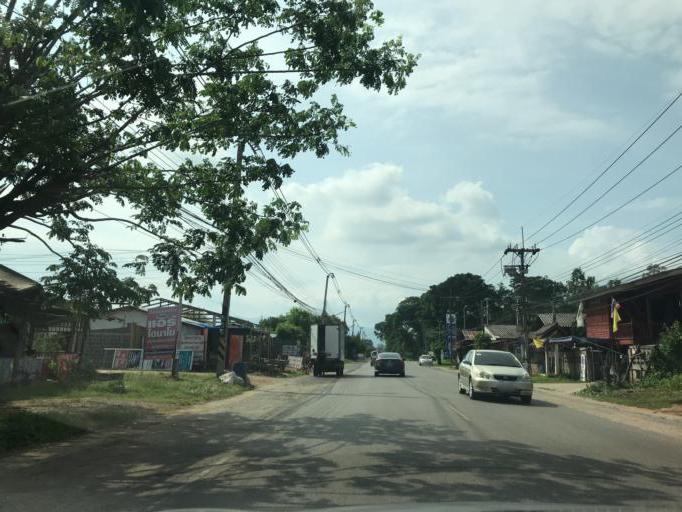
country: TH
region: Phayao
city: Chiang Kham
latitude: 19.5172
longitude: 100.3124
